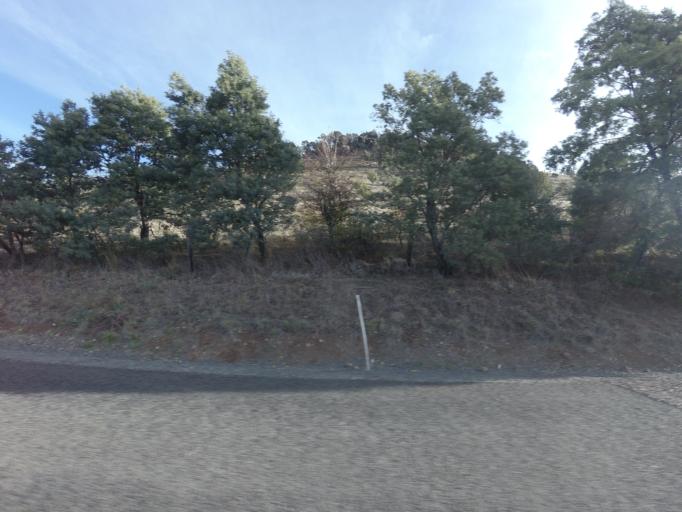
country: AU
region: Tasmania
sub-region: Brighton
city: Bridgewater
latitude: -42.4187
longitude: 147.1392
